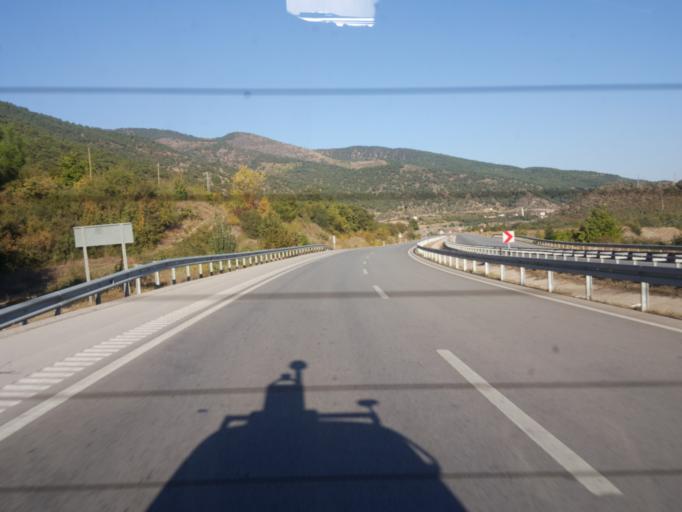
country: TR
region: Amasya
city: Tekke
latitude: 40.7470
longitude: 36.1280
